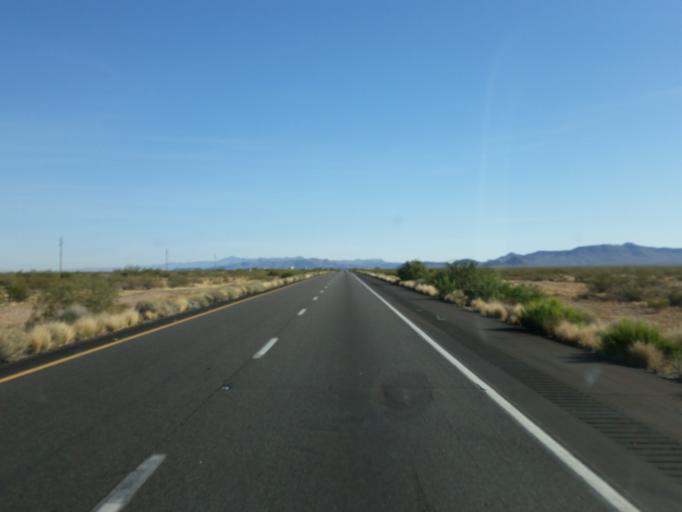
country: US
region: Arizona
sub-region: Mohave County
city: Kingman
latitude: 34.9924
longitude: -114.1378
